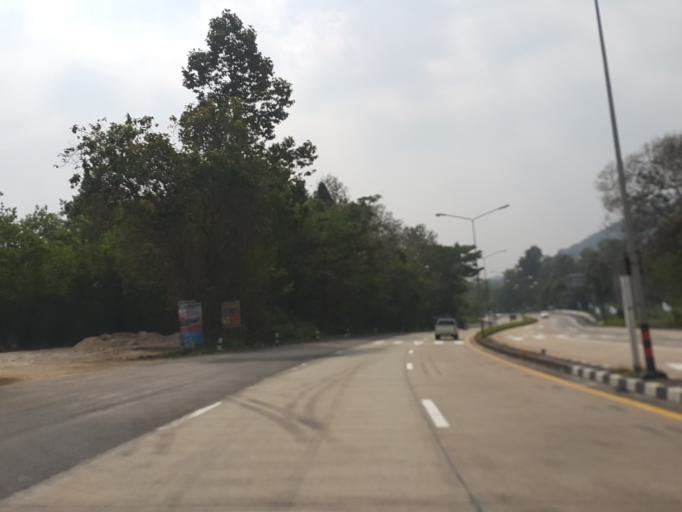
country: TH
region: Lampang
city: Hang Chat
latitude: 18.3540
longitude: 99.2433
